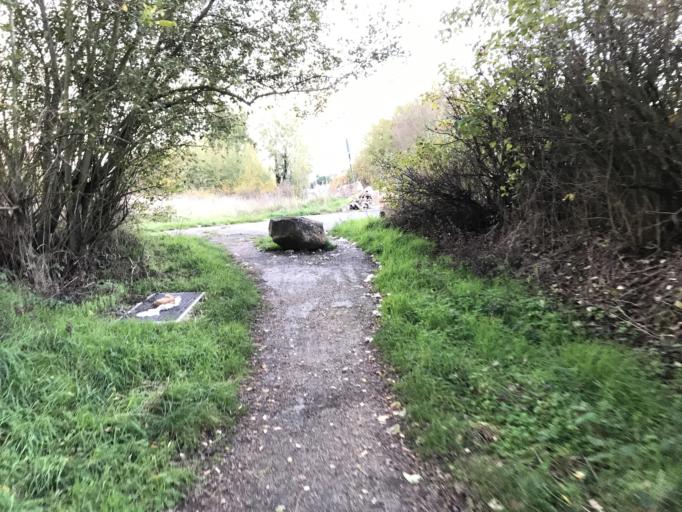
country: FR
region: Ile-de-France
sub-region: Departement de l'Essonne
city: Saulx-les-Chartreux
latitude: 48.6768
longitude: 2.2778
